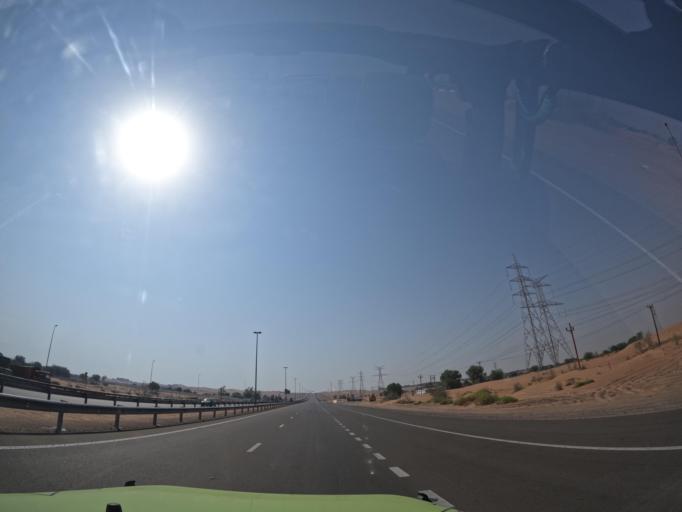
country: OM
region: Al Buraimi
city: Al Buraymi
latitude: 24.3611
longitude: 55.7314
